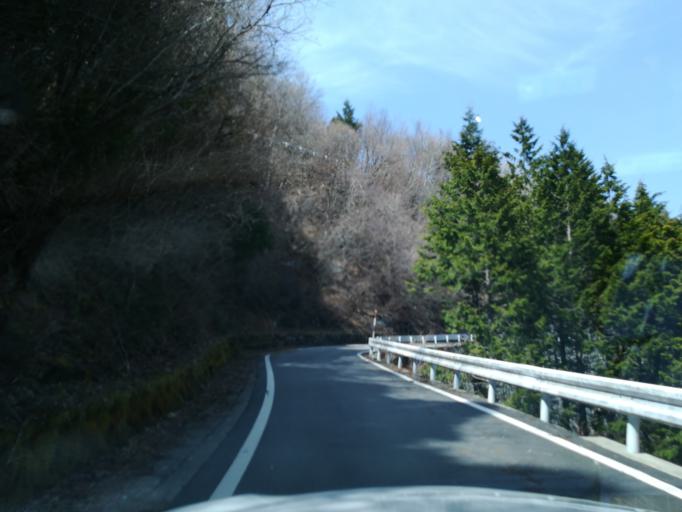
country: JP
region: Tokushima
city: Wakimachi
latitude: 33.8795
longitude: 134.0517
